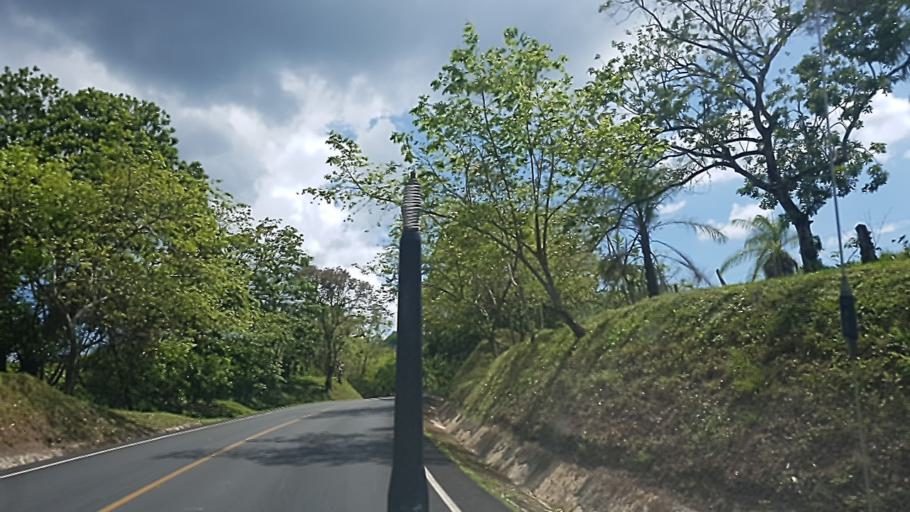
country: NI
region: Atlantico Sur
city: Muelle de los Bueyes
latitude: 11.9838
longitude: -84.7576
